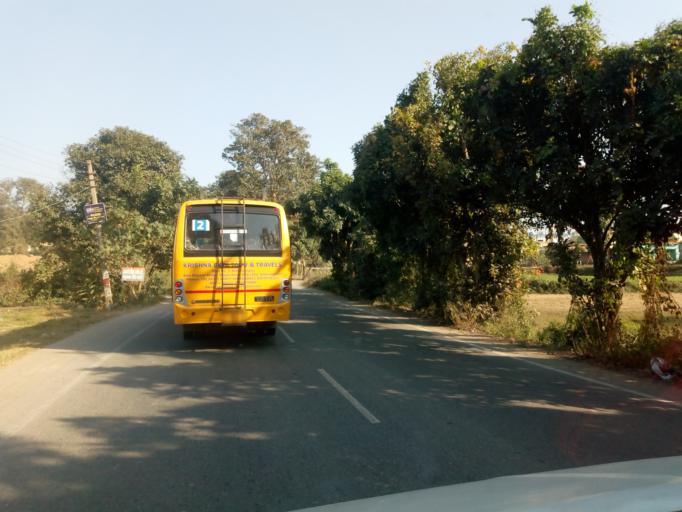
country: IN
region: Uttarakhand
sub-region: Dehradun
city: Dehradun
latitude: 30.3494
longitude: 77.8876
